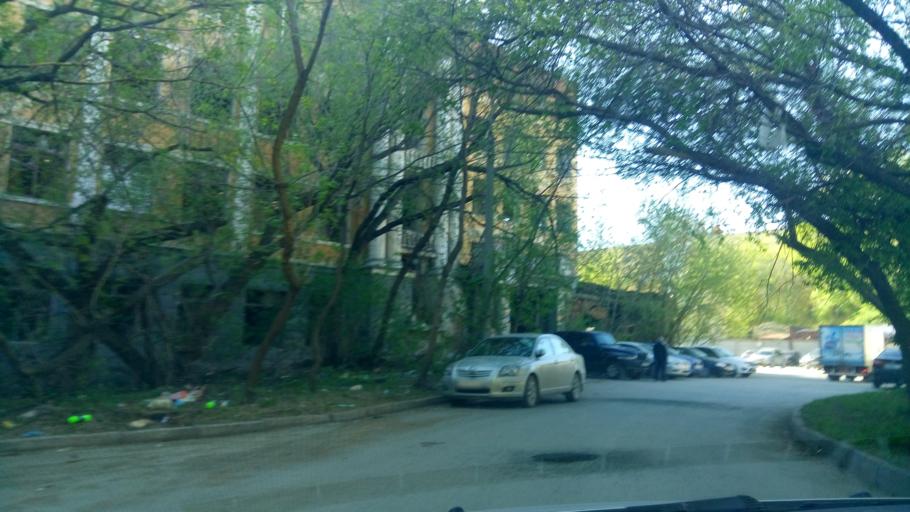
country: RU
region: Sverdlovsk
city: Yekaterinburg
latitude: 56.8197
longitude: 60.6017
